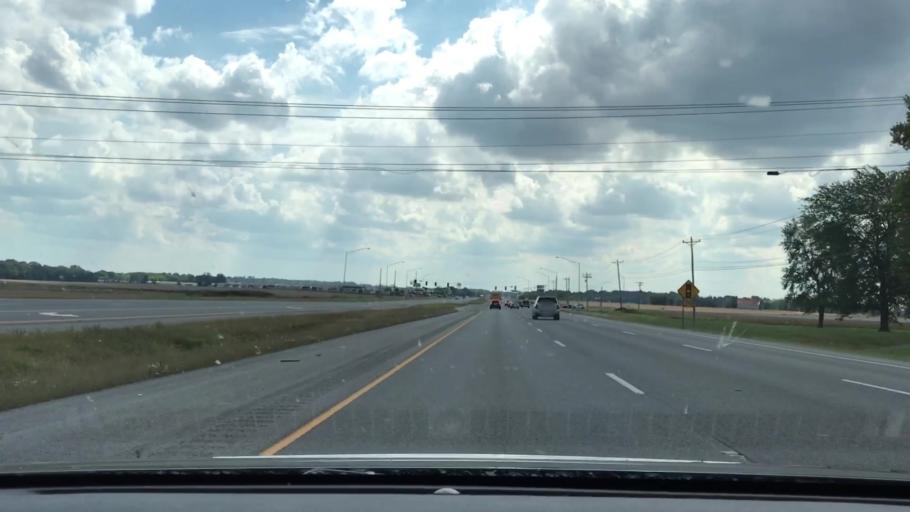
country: US
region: Kentucky
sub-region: Christian County
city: Oak Grove
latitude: 36.6785
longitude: -87.4471
